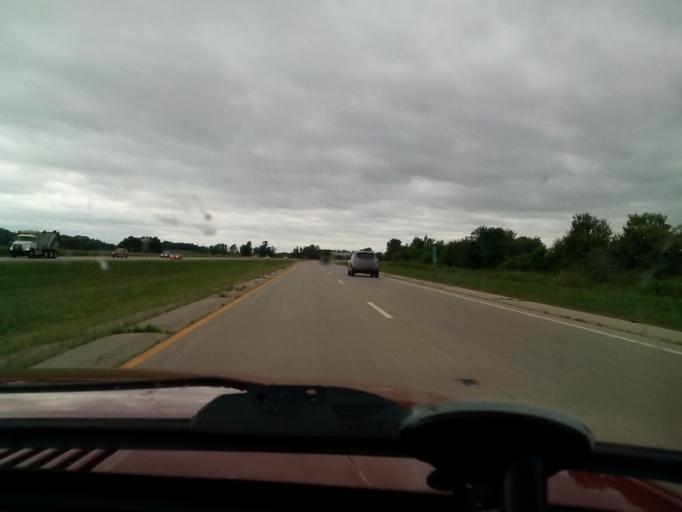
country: US
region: Wisconsin
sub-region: Columbia County
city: Columbus
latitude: 43.2825
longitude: -89.0825
